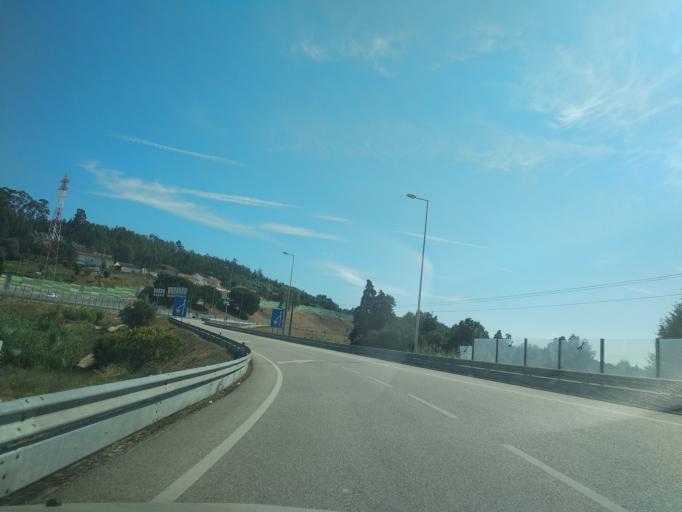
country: PT
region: Coimbra
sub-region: Coimbra
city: Coimbra
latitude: 40.1994
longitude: -8.4894
